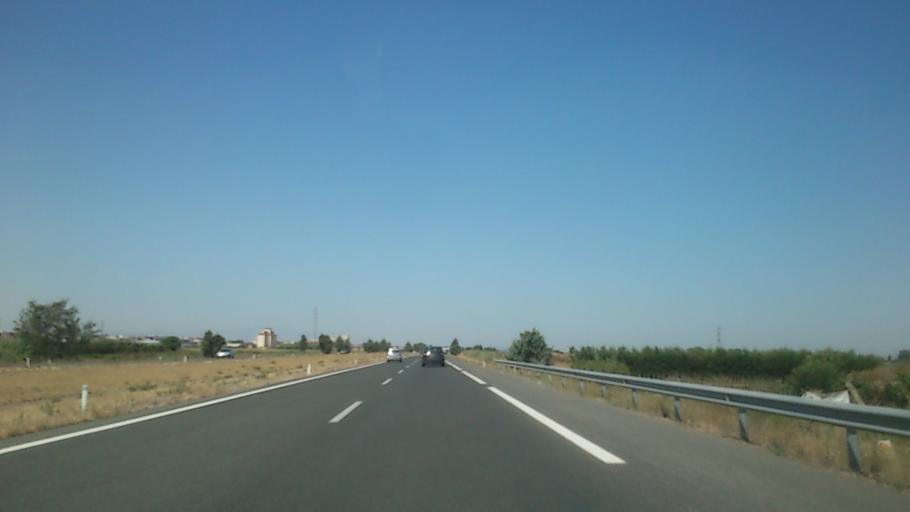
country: ES
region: Aragon
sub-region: Provincia de Zaragoza
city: Utebo
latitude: 41.7200
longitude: -1.0002
